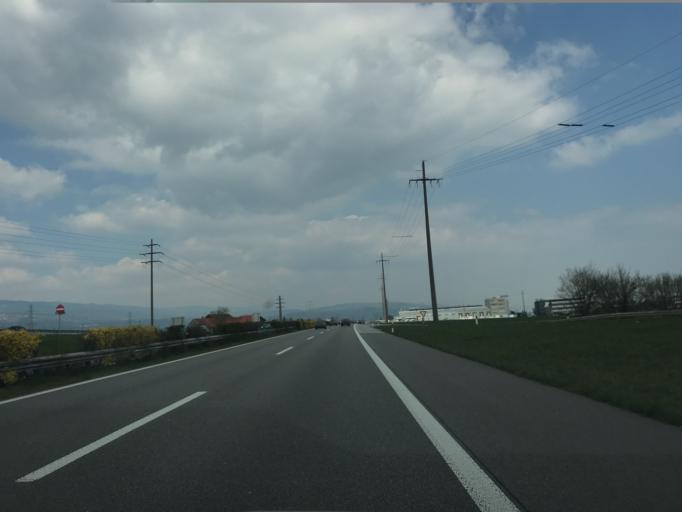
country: CH
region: Vaud
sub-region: Nyon District
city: Trelex
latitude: 46.3959
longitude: 6.2102
